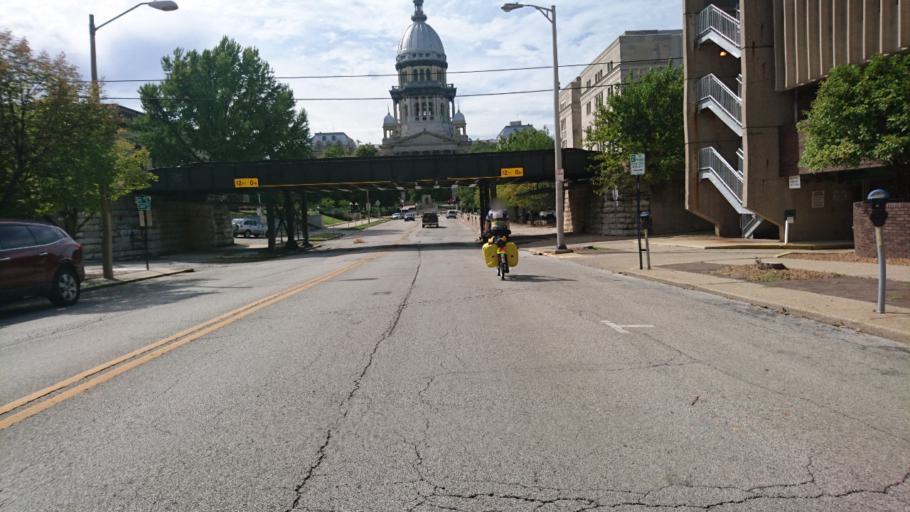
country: US
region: Illinois
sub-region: Sangamon County
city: Springfield
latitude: 39.7985
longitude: -89.6514
